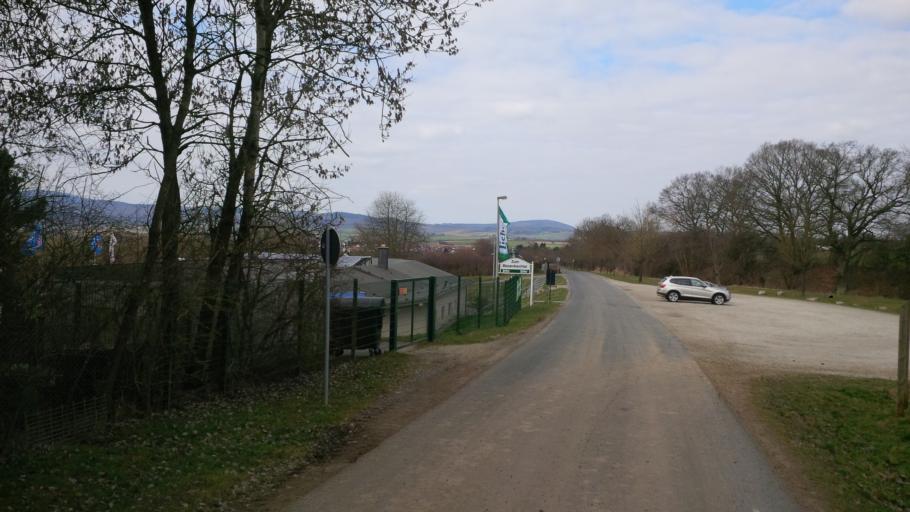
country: DE
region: Hesse
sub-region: Regierungsbezirk Darmstadt
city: Wehrheim
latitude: 50.3038
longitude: 8.5882
